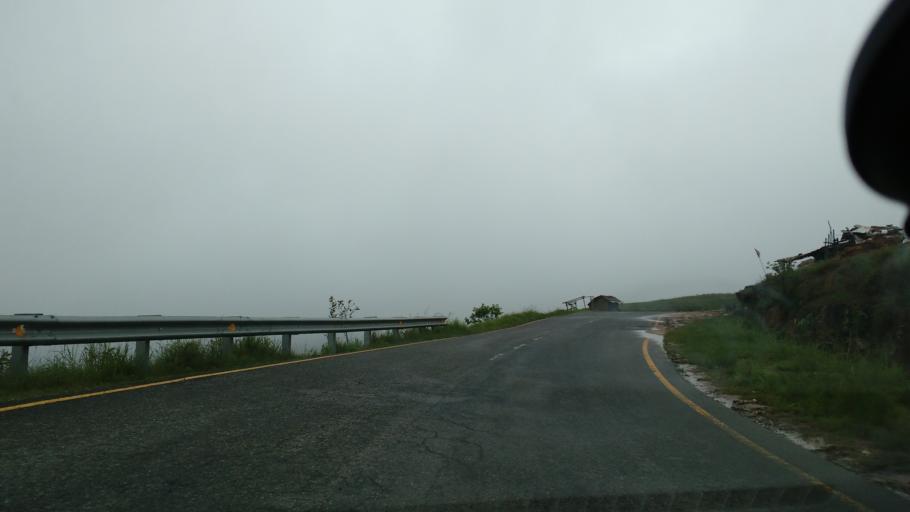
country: IN
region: Meghalaya
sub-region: East Khasi Hills
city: Cherrapunji
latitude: 25.3178
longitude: 91.7341
